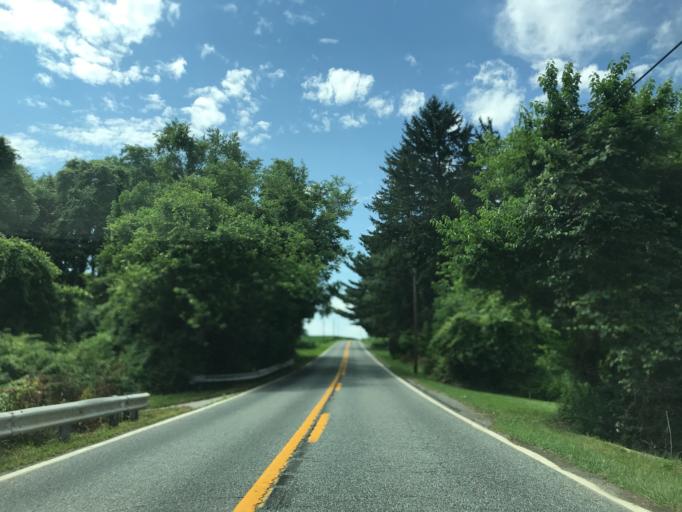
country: US
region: Pennsylvania
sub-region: York County
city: Susquehanna Trails
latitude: 39.7135
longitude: -76.4319
